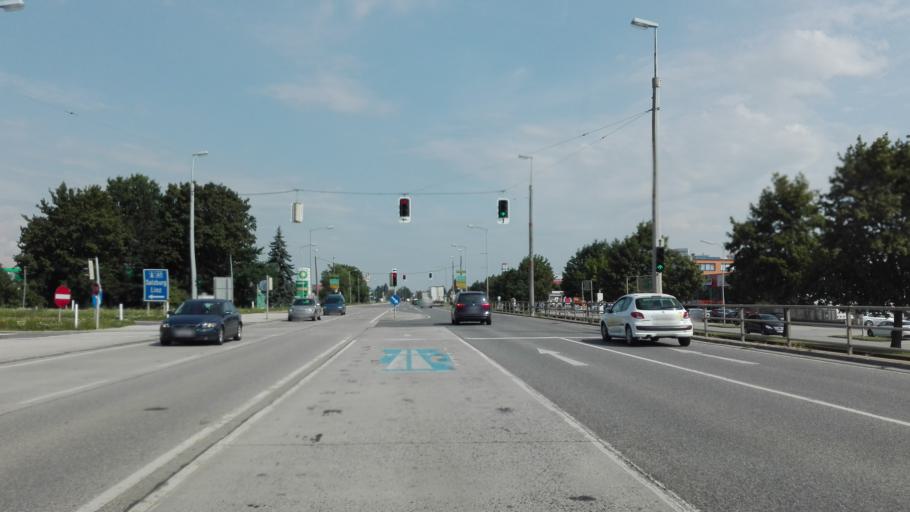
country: AT
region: Lower Austria
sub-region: Sankt Polten Stadt
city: Sankt Poelten
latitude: 48.1780
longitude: 15.6162
